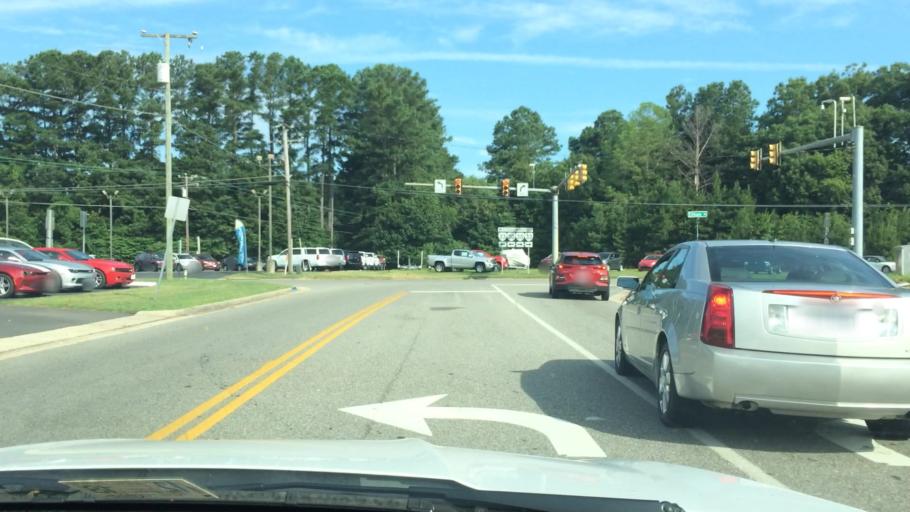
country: US
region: Virginia
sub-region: King William County
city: West Point
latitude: 37.5235
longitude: -76.8262
